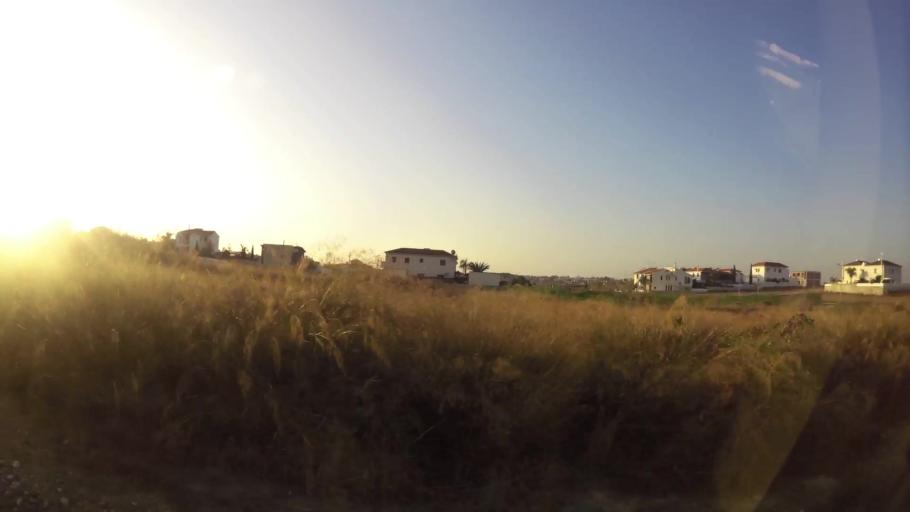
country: CY
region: Larnaka
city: Aradippou
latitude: 34.9238
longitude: 33.5872
